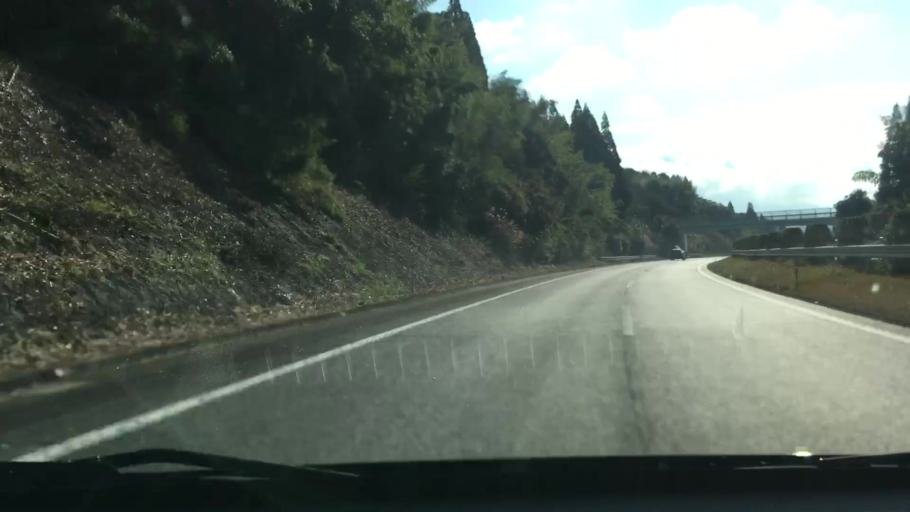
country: JP
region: Kumamoto
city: Matsubase
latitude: 32.6092
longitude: 130.7244
